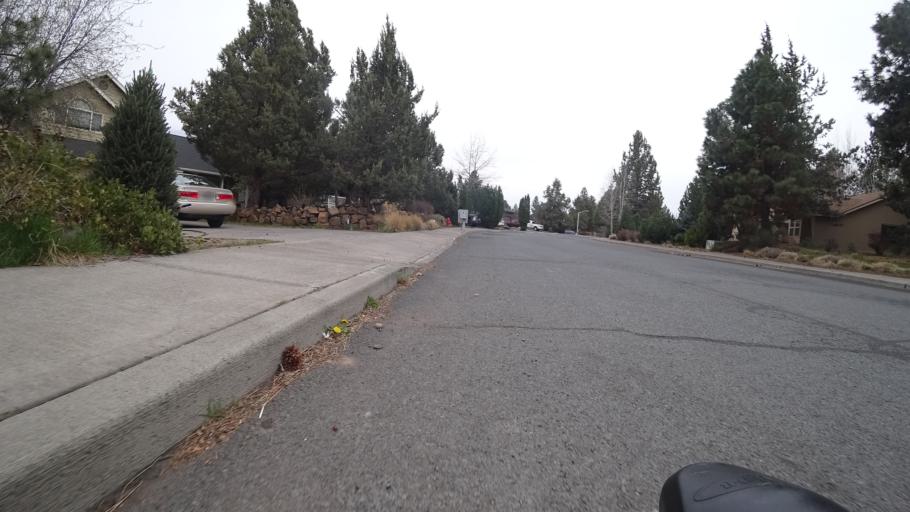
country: US
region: Oregon
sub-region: Deschutes County
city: Bend
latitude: 44.0386
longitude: -121.2746
